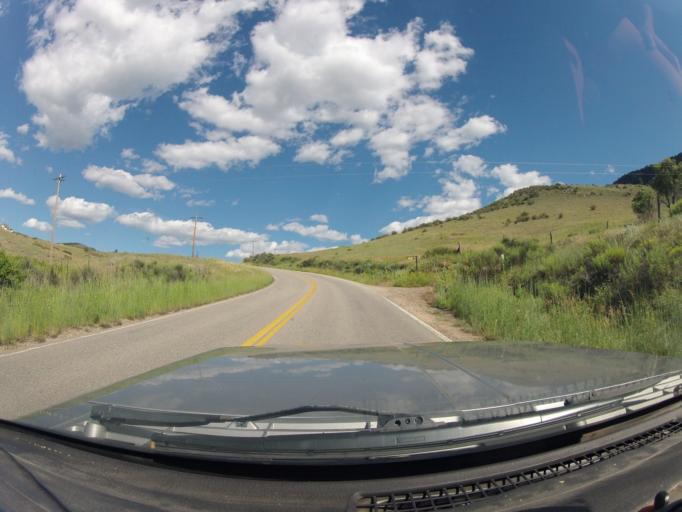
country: US
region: Colorado
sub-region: Larimer County
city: Laporte
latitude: 40.5318
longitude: -105.2685
